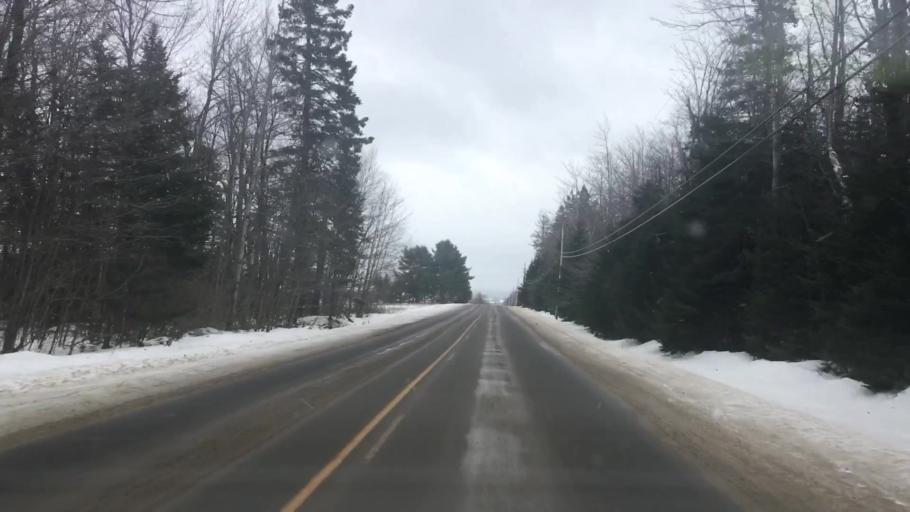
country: US
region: Maine
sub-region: Washington County
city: East Machias
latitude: 44.9829
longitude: -67.4553
